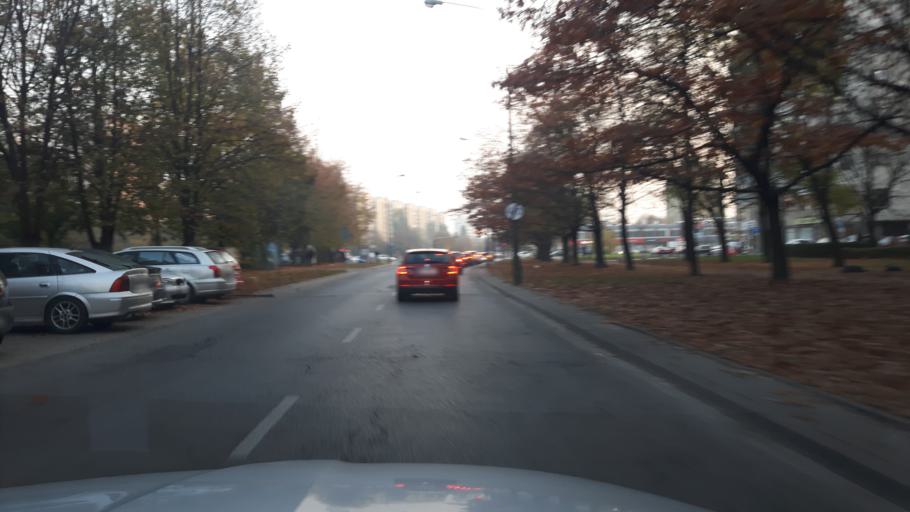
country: PL
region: Masovian Voivodeship
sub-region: Warszawa
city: Mokotow
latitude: 52.1813
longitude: 21.0141
